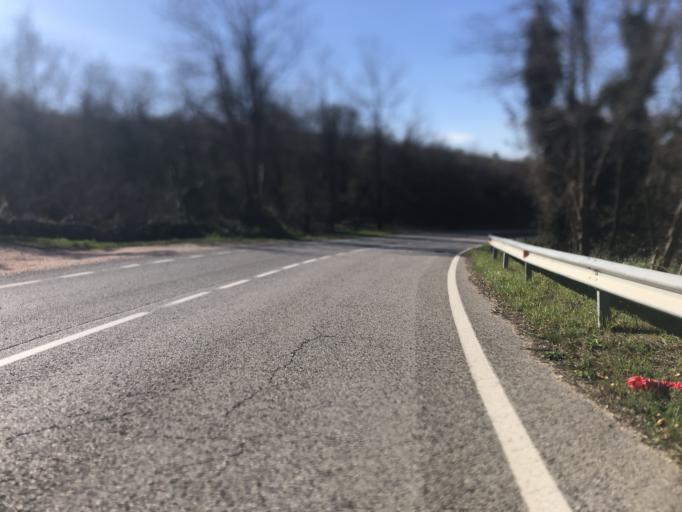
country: IT
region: Veneto
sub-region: Provincia di Verona
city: Volargne
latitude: 45.5402
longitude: 10.8337
